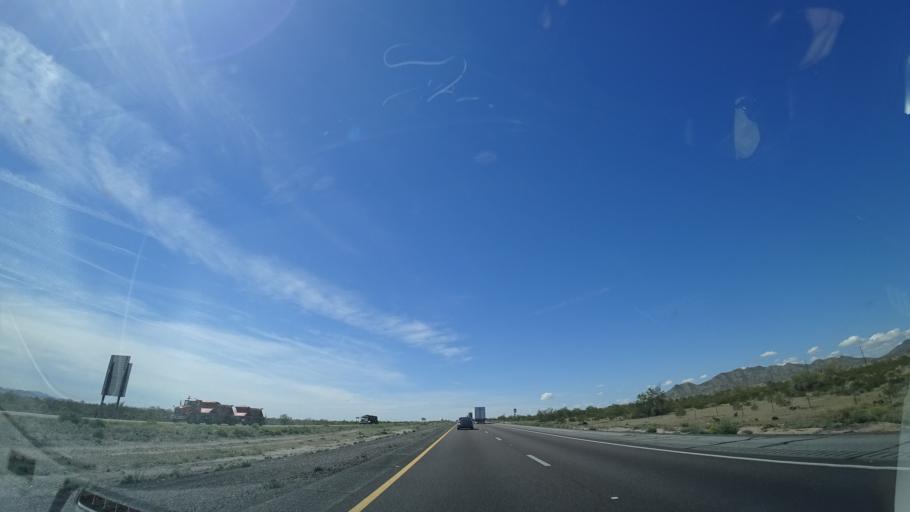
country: US
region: Arizona
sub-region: Maricopa County
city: Buckeye
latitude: 33.4557
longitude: -112.5231
